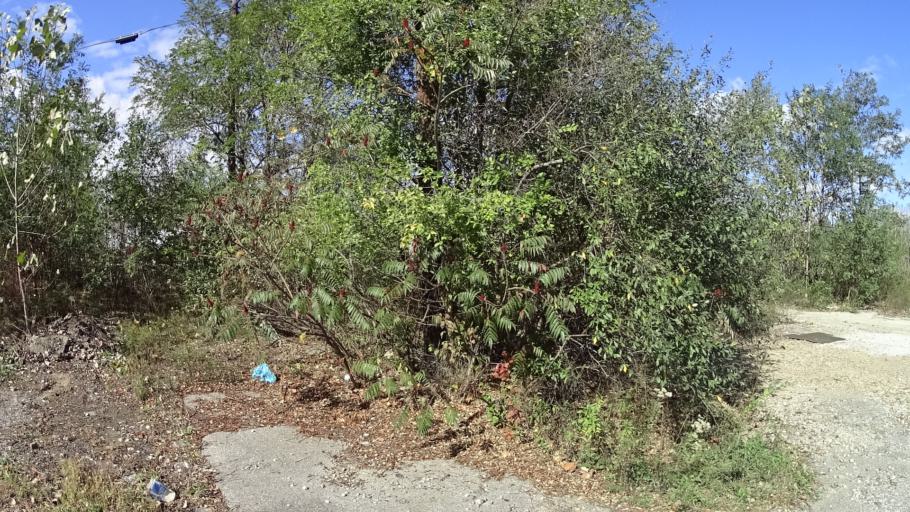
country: US
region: Ohio
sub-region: Lorain County
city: Grafton
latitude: 41.2778
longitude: -82.0540
